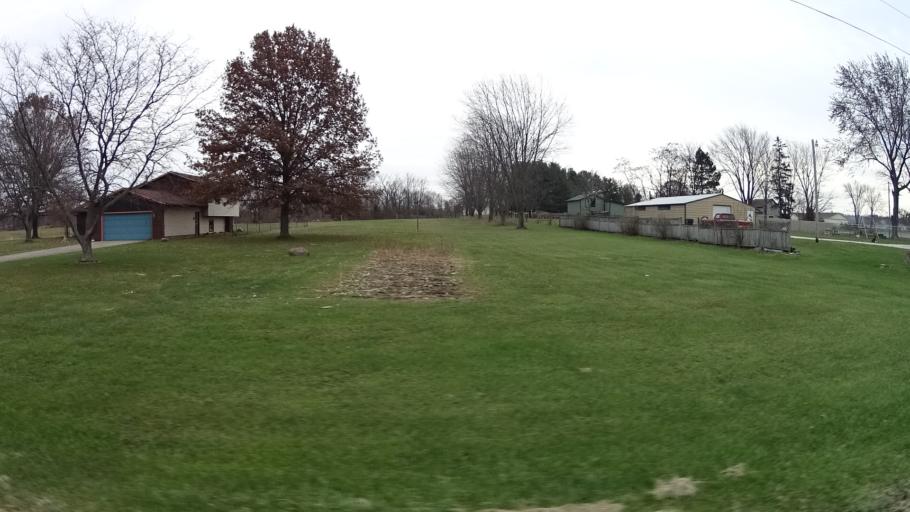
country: US
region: Ohio
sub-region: Lorain County
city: Lagrange
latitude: 41.1691
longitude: -82.0835
